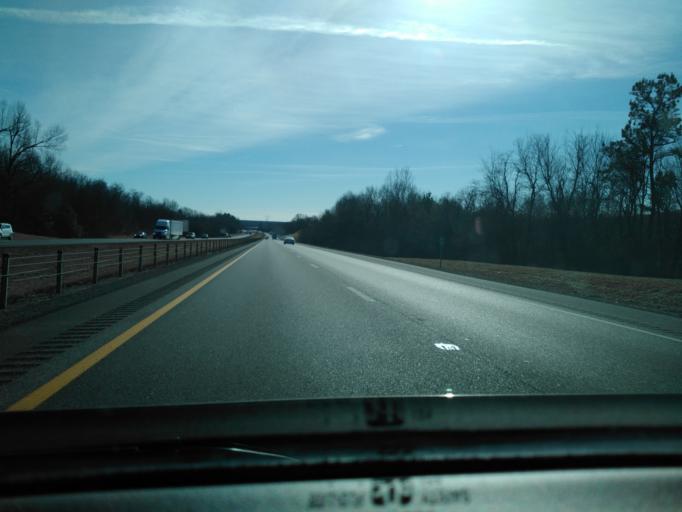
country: US
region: Kentucky
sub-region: McCracken County
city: Hendron
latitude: 37.0403
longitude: -88.6370
